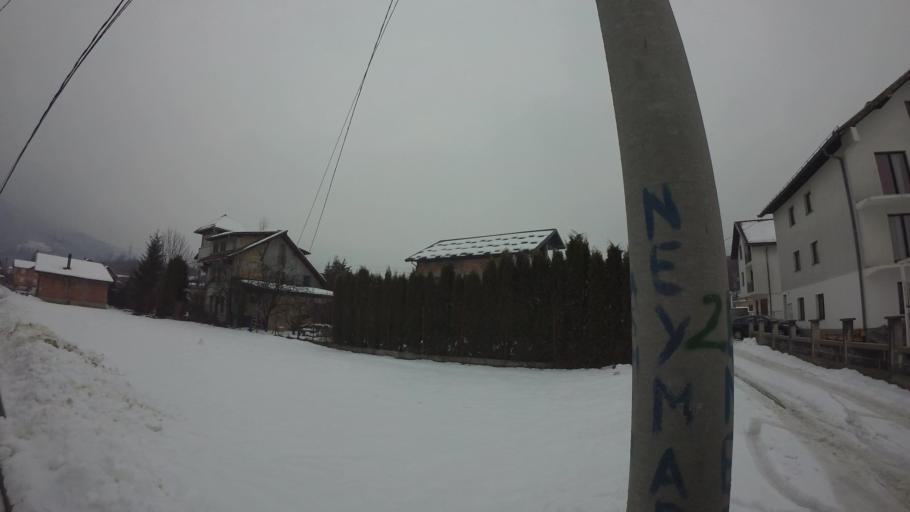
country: BA
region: Federation of Bosnia and Herzegovina
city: Hadzici
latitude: 43.8422
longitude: 18.2717
